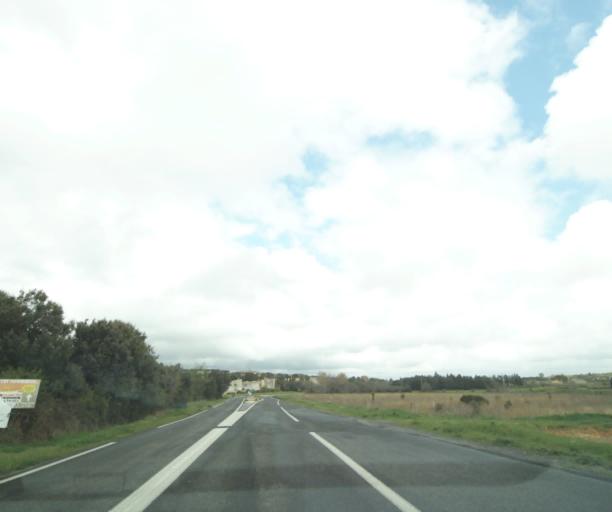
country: FR
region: Languedoc-Roussillon
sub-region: Departement de l'Herault
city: Cournonsec
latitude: 43.5392
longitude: 3.6992
